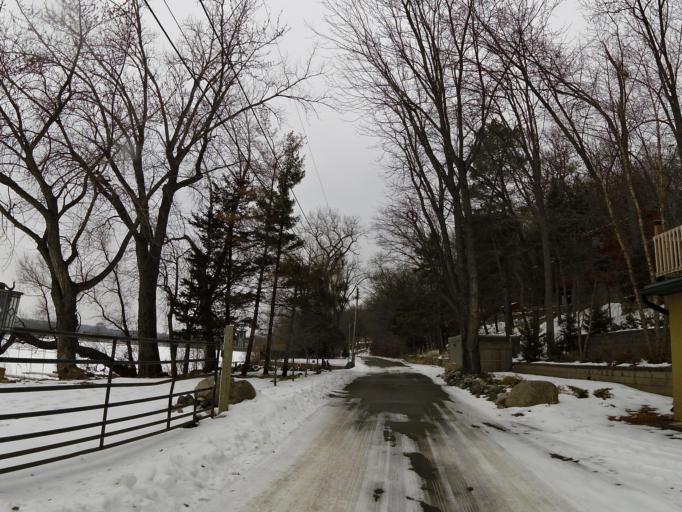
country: US
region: Minnesota
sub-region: Washington County
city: Lakeland
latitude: 44.9581
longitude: -92.7484
